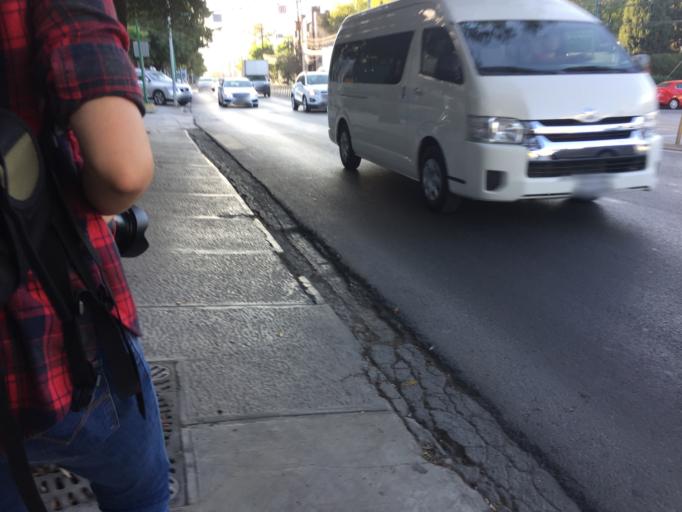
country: MX
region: Nuevo Leon
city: Garza Garcia
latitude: 25.6517
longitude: -100.3670
